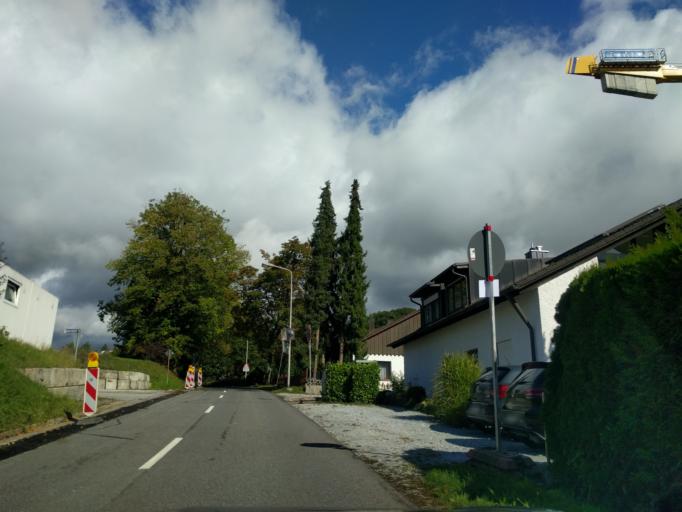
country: DE
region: Bavaria
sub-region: Lower Bavaria
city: Deggendorf
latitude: 48.8339
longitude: 12.9756
